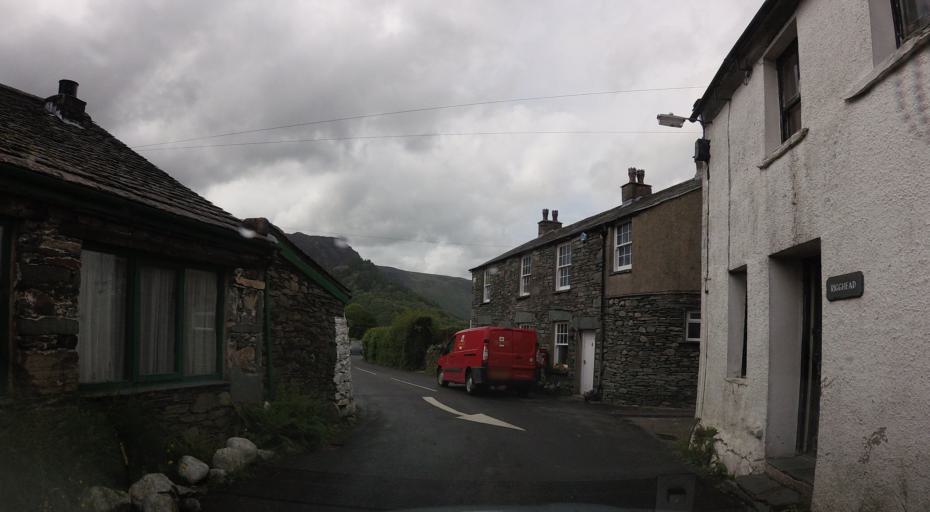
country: GB
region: England
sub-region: Cumbria
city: Keswick
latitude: 54.5239
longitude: -3.1470
